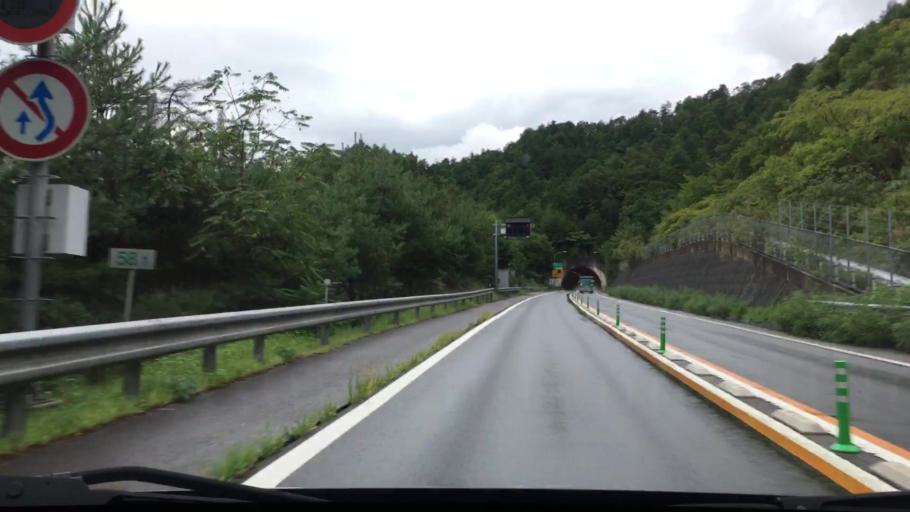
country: JP
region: Hyogo
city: Toyooka
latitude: 35.2767
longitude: 134.8156
